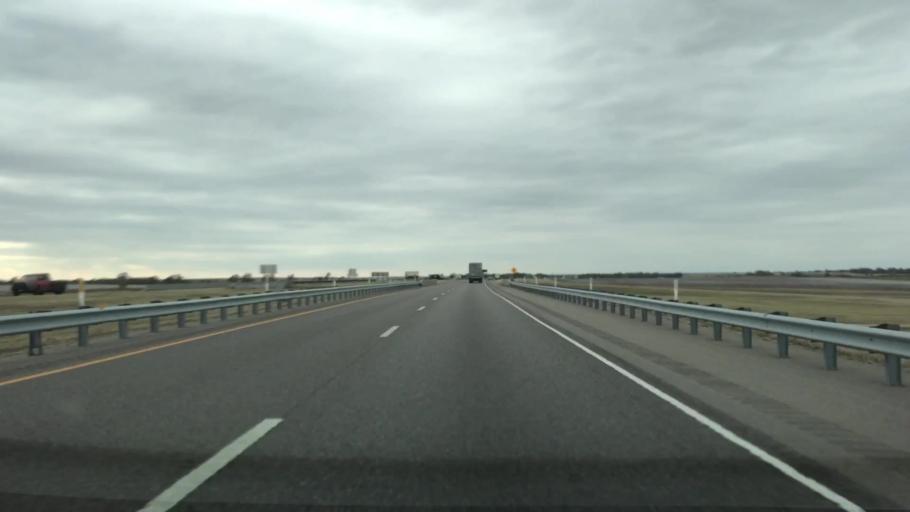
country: US
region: Oklahoma
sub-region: Beckham County
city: Erick
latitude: 35.2280
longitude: -99.9903
